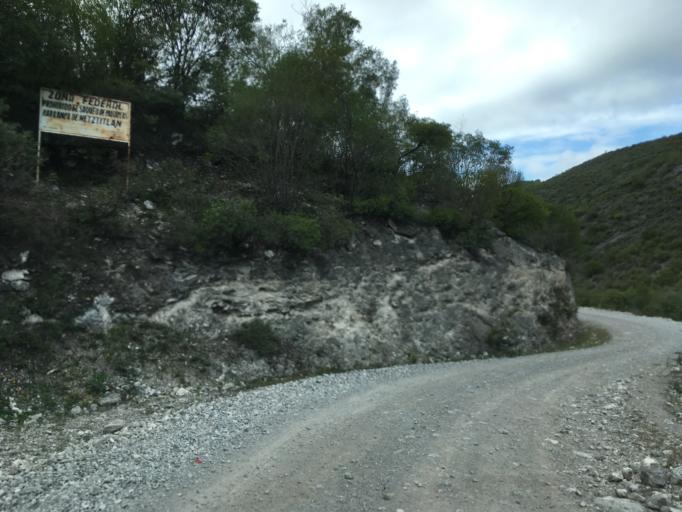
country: MX
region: Hidalgo
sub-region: Metztitlan
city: Fontezuelas
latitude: 20.6227
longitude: -98.8718
